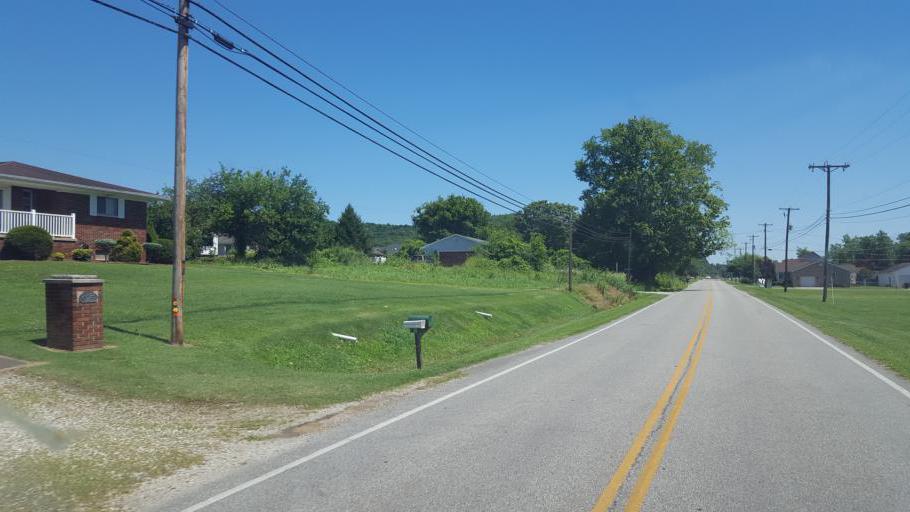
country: US
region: West Virginia
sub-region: Cabell County
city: Pea Ridge
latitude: 38.4561
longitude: -82.3237
